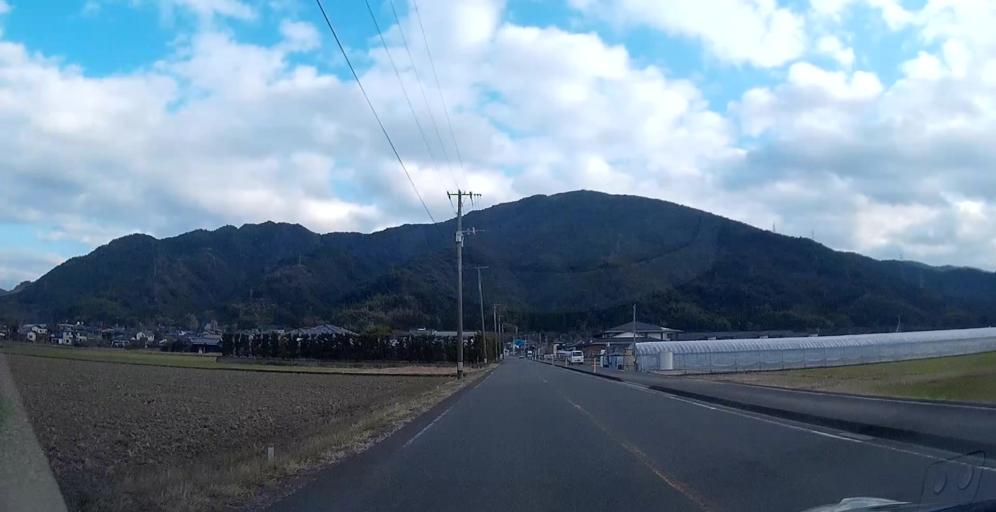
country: JP
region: Kumamoto
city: Yatsushiro
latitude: 32.5292
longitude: 130.6580
